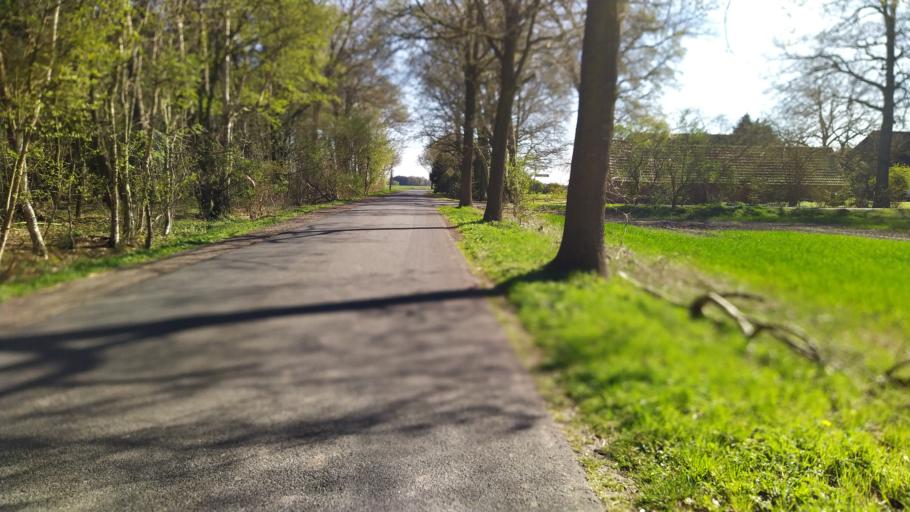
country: DE
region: Lower Saxony
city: Heeslingen
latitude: 53.3229
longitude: 9.3902
